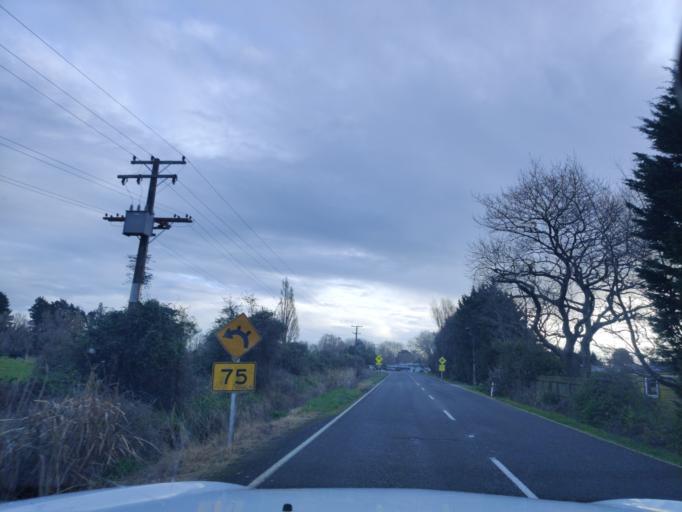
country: NZ
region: Manawatu-Wanganui
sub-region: Palmerston North City
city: Palmerston North
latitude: -40.3632
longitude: 175.6676
